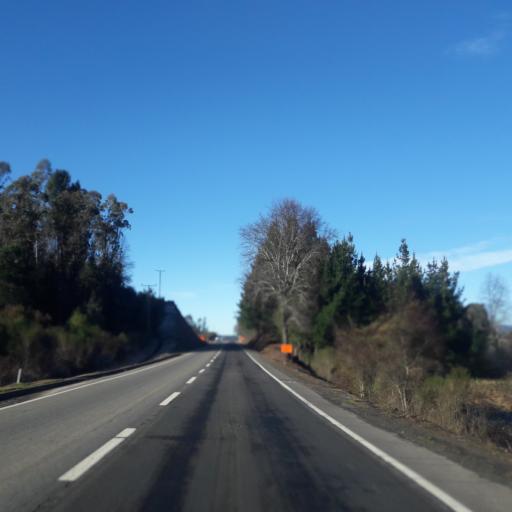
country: CL
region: Biobio
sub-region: Provincia de Biobio
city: La Laja
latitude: -37.3002
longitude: -72.9285
